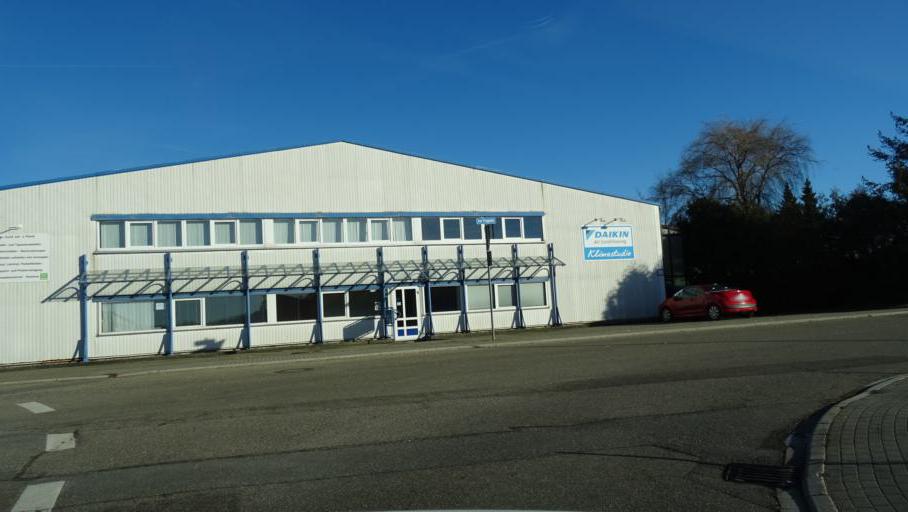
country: DE
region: Baden-Wuerttemberg
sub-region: Karlsruhe Region
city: Fahrenbach
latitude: 49.3947
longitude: 9.1247
